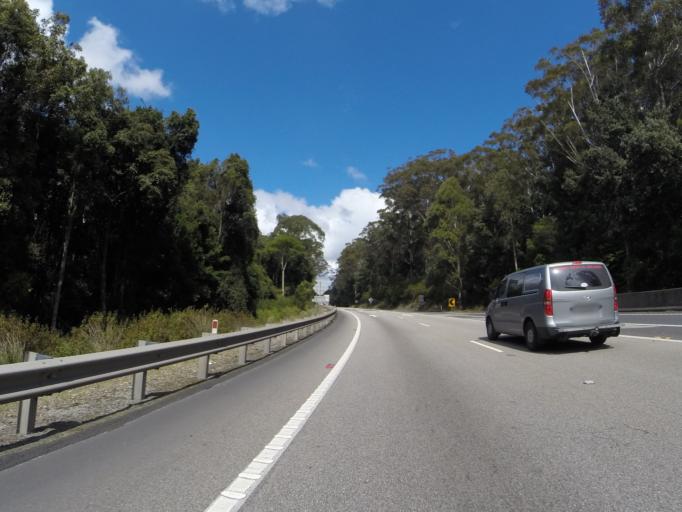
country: AU
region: New South Wales
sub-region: Wollongong
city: Mount Ousley
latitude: -34.3646
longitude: 150.8512
